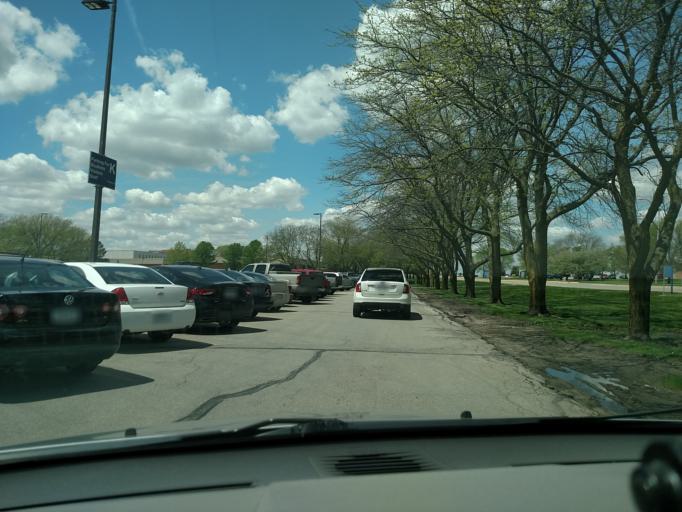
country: US
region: Iowa
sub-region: Polk County
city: Ankeny
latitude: 41.7078
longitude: -93.6085
